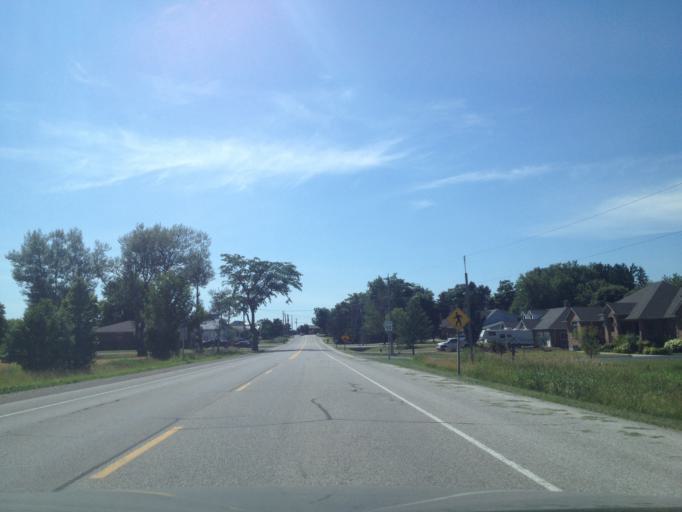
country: CA
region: Ontario
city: Waterloo
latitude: 43.5274
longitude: -80.7391
